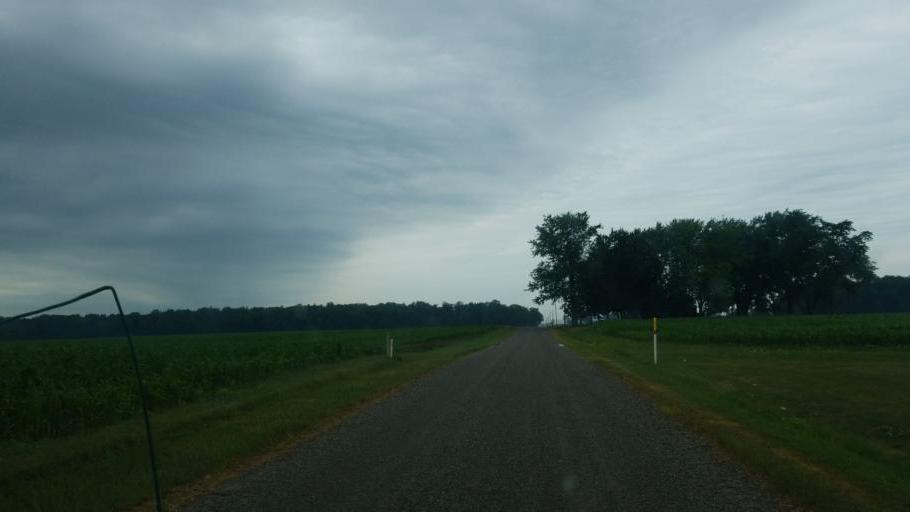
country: US
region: Indiana
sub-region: DeKalb County
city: Butler
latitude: 41.4613
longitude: -84.9100
